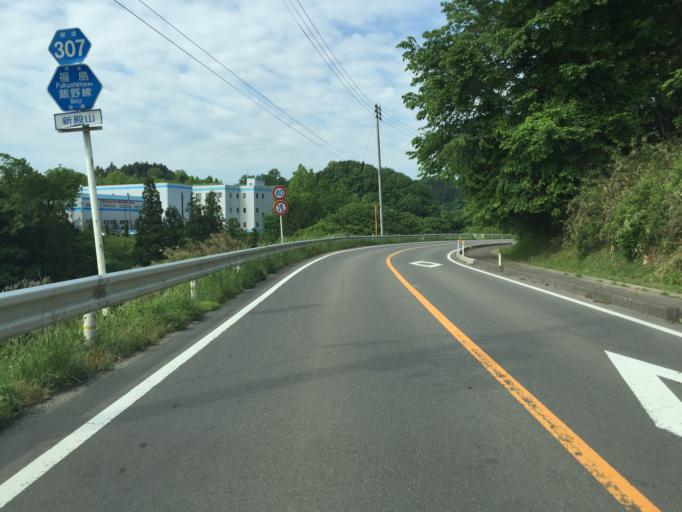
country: JP
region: Fukushima
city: Fukushima-shi
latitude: 37.6602
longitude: 140.5111
